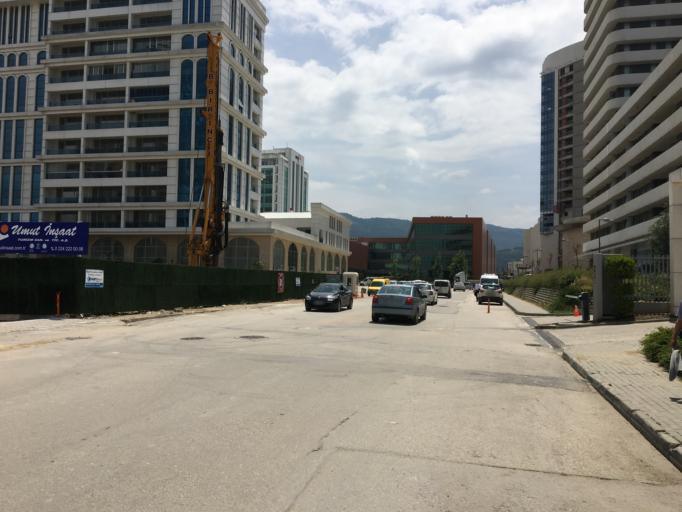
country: TR
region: Bursa
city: Yildirim
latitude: 40.2094
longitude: 28.9974
